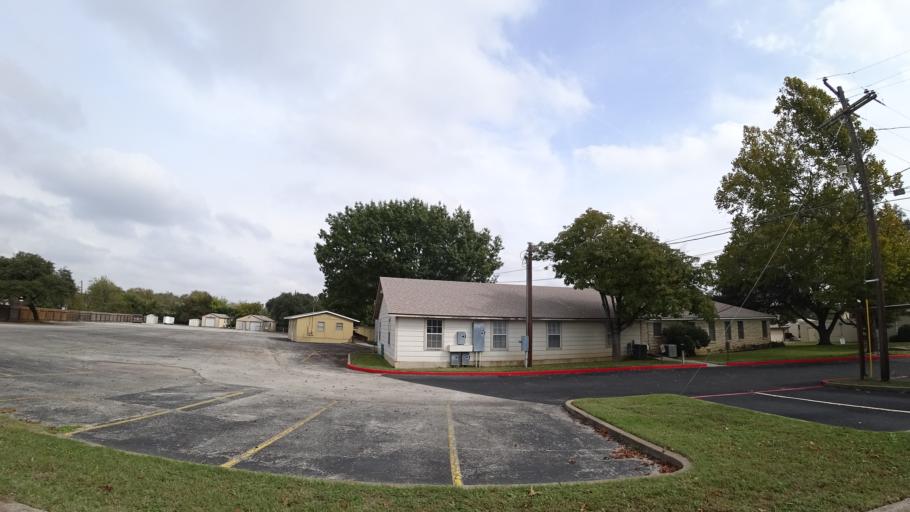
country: US
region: Texas
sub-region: Williamson County
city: Round Rock
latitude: 30.4953
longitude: -97.6927
